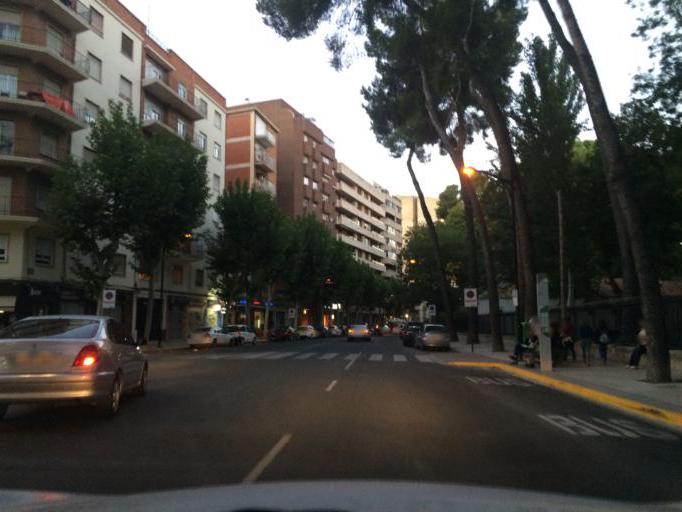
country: ES
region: Castille-La Mancha
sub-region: Provincia de Albacete
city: Albacete
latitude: 38.9864
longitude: -1.8590
